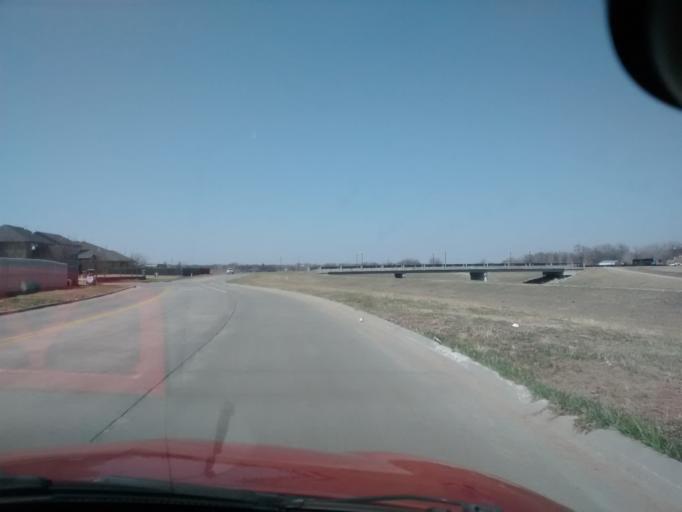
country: US
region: Nebraska
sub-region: Sarpy County
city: Offutt Air Force Base
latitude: 41.1445
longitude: -95.9770
